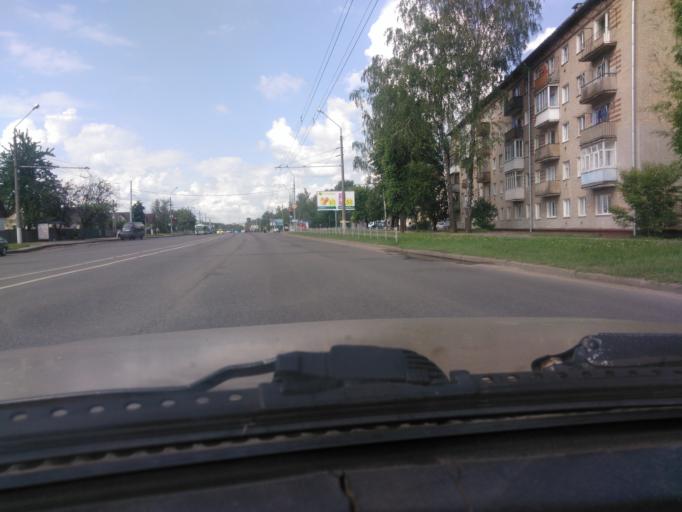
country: BY
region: Mogilev
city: Mahilyow
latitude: 53.9359
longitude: 30.3533
